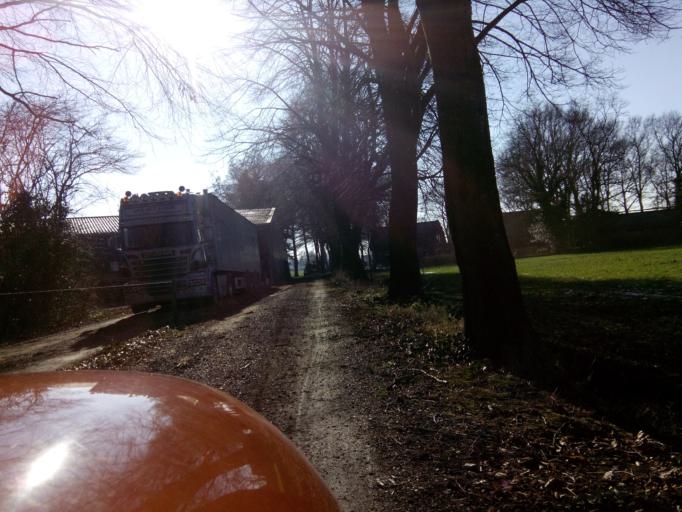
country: NL
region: Gelderland
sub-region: Gemeente Barneveld
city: Barneveld
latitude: 52.1314
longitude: 5.5541
